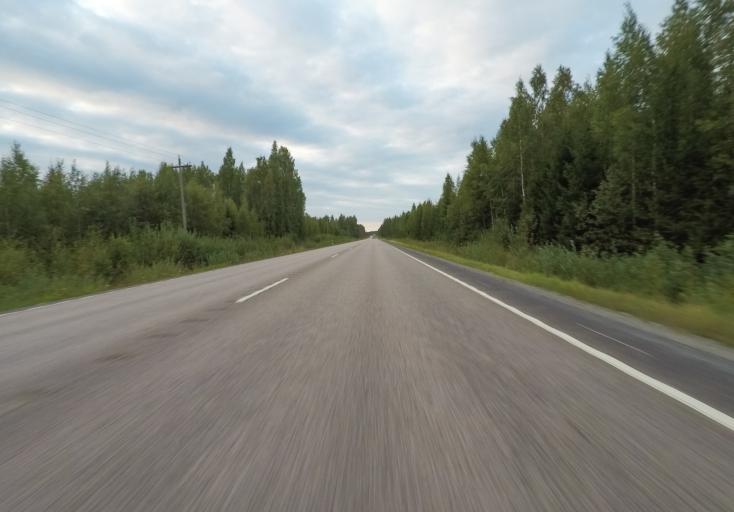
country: FI
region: Central Finland
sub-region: Joutsa
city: Leivonmaeki
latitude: 61.9407
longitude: 26.1122
